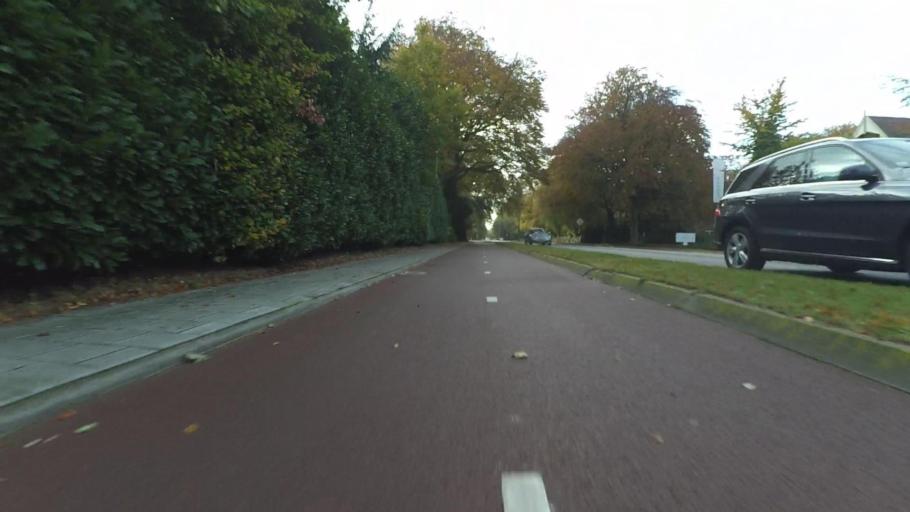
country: NL
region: Utrecht
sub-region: Gemeente Baarn
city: Baarn
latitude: 52.2108
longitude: 5.2691
